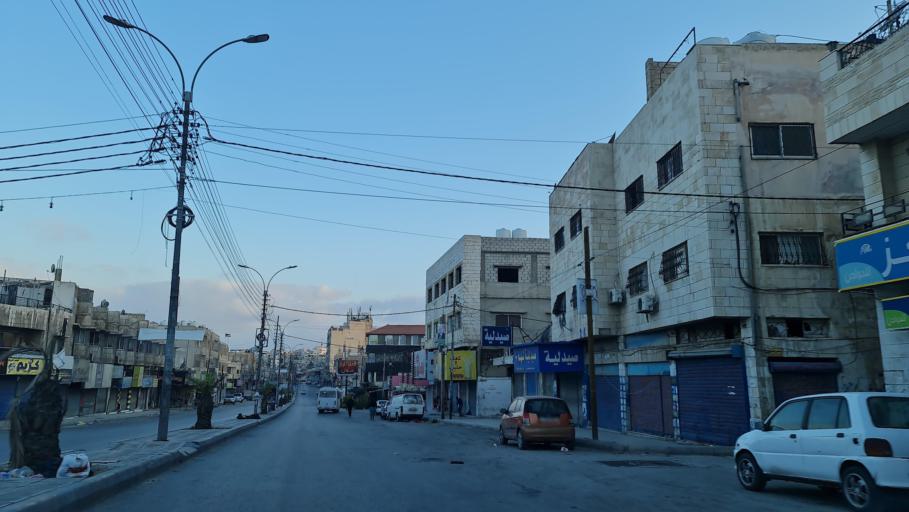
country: JO
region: Zarqa
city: Zarqa
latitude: 32.0759
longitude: 36.0773
